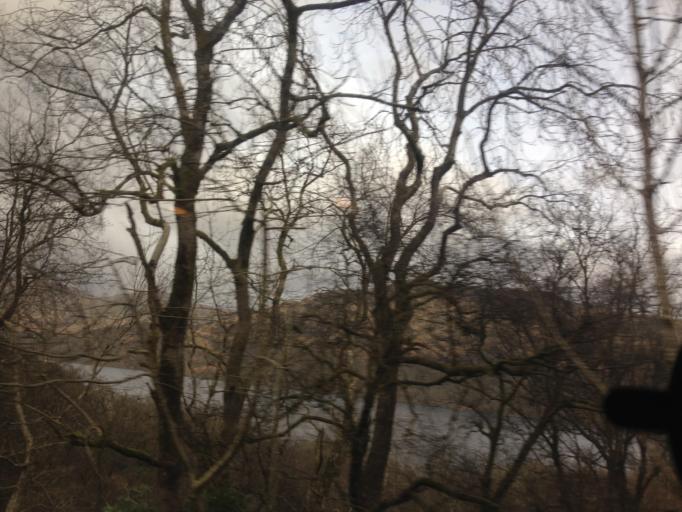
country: GB
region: Scotland
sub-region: Argyll and Bute
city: Garelochhead
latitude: 56.2164
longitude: -4.6988
